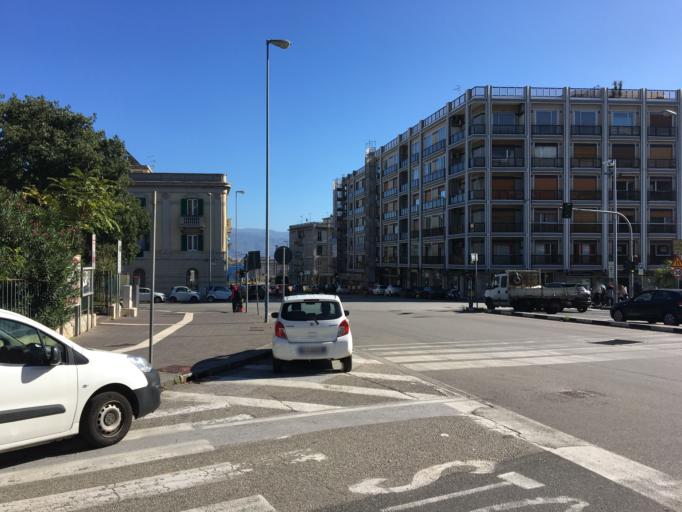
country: IT
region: Sicily
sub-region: Messina
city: Messina
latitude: 38.1976
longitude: 15.5560
